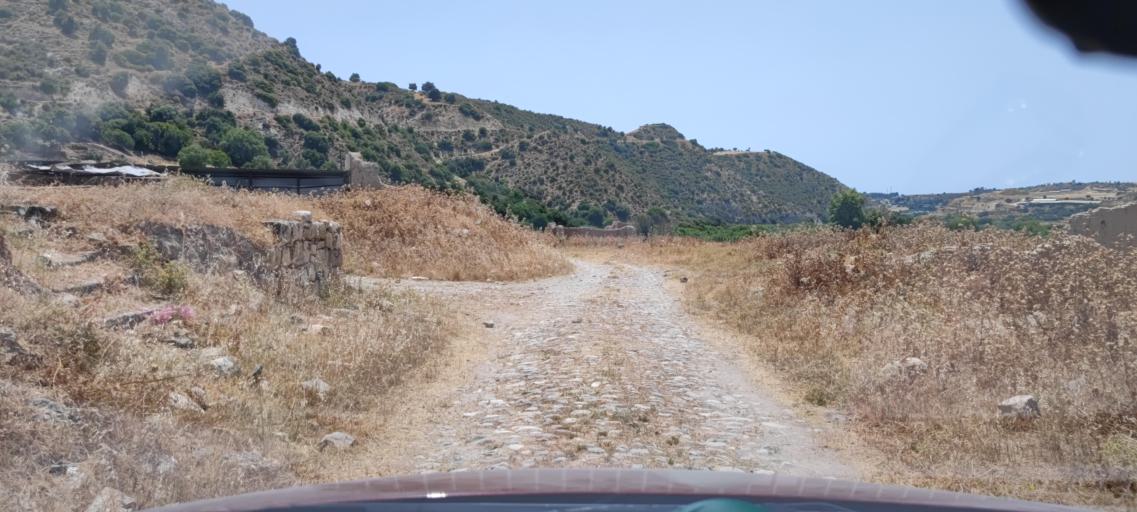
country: CY
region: Limassol
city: Pissouri
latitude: 34.7328
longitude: 32.6017
